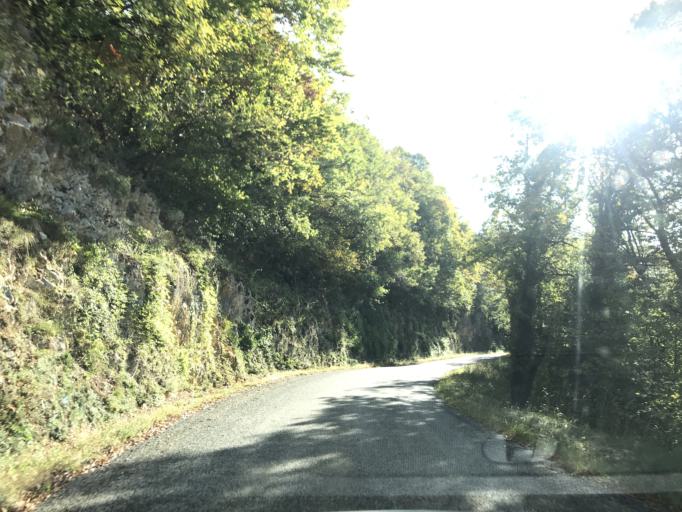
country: FR
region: Rhone-Alpes
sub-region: Departement de la Savoie
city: Novalaise
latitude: 45.6394
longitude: 5.7975
